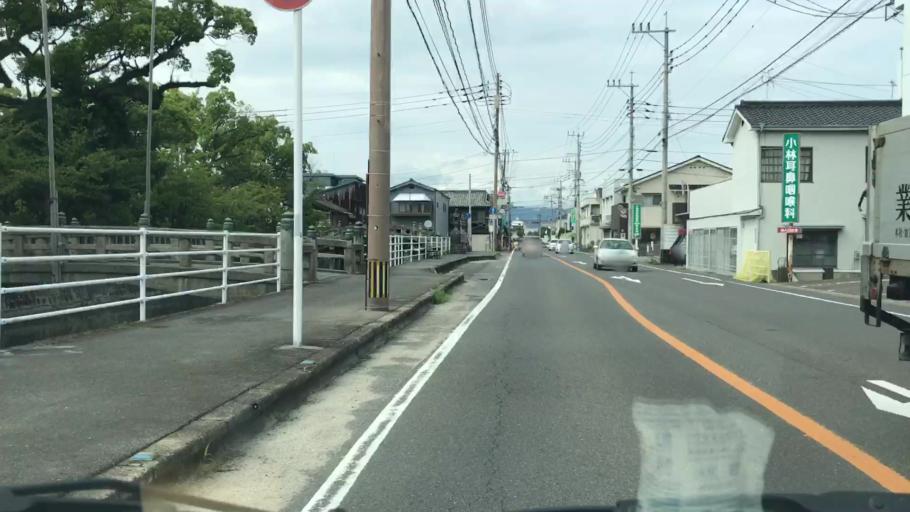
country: JP
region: Saga Prefecture
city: Saga-shi
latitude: 33.2527
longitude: 130.2935
